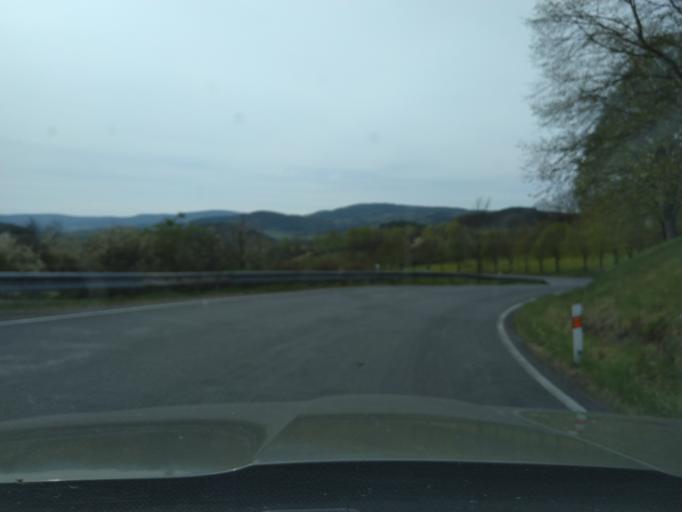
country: CZ
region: Plzensky
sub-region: Okres Klatovy
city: Susice
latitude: 49.2420
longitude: 13.5773
